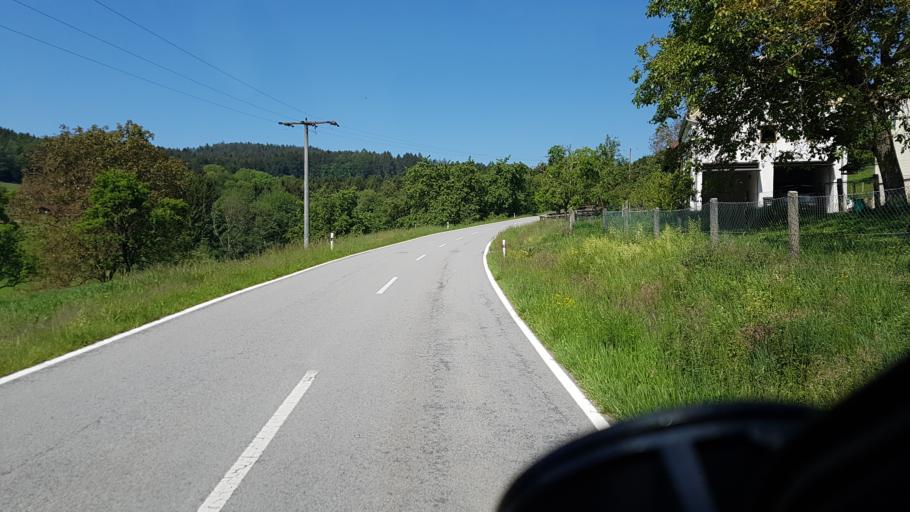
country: DE
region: Bavaria
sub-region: Lower Bavaria
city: Stubenberg
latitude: 48.2931
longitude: 13.0568
